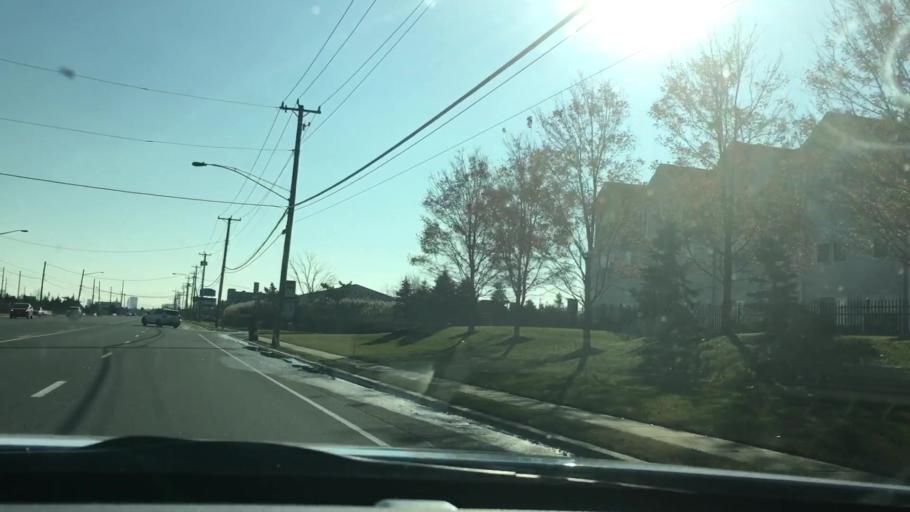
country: US
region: New Jersey
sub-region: Atlantic County
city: Pleasantville
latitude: 39.3797
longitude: -74.4932
